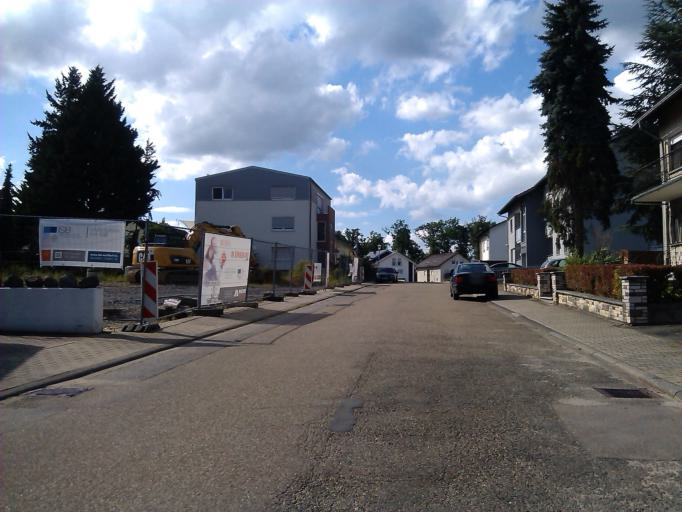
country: DE
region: Baden-Wuerttemberg
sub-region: Karlsruhe Region
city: Ostringen
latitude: 49.2249
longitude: 8.7233
